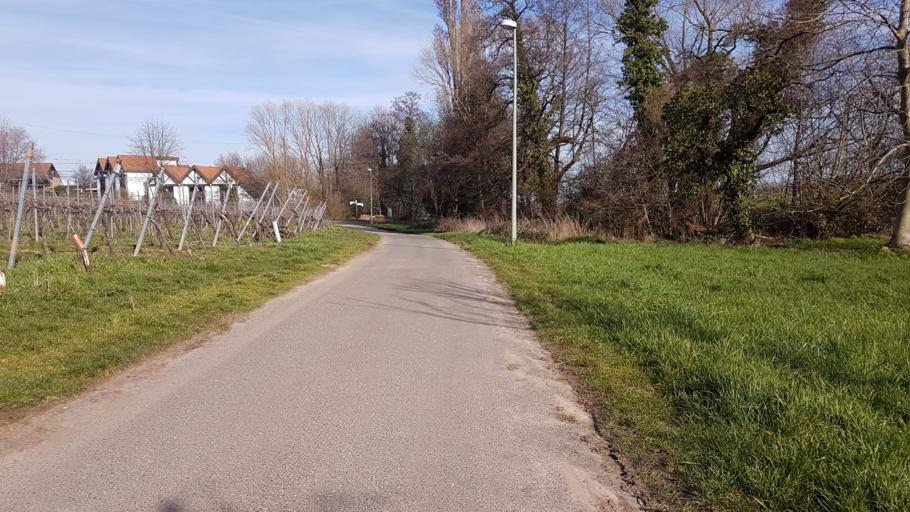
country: DE
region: Rheinland-Pfalz
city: Maikammer
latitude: 49.2987
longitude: 8.1222
